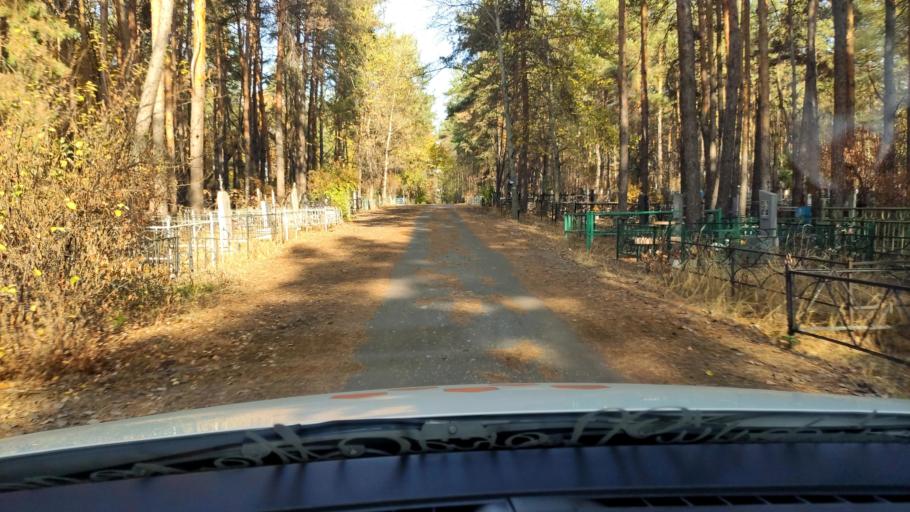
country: RU
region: Voronezj
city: Pridonskoy
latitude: 51.6672
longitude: 39.0953
